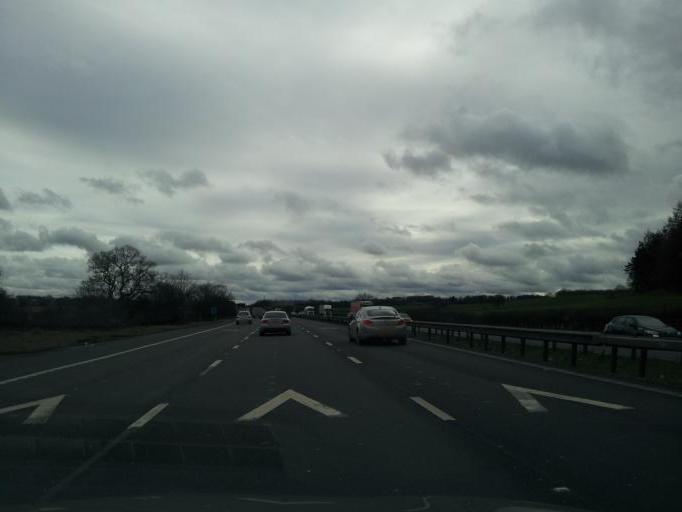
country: GB
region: England
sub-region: Staffordshire
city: Barlaston
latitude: 52.9351
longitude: -2.2139
